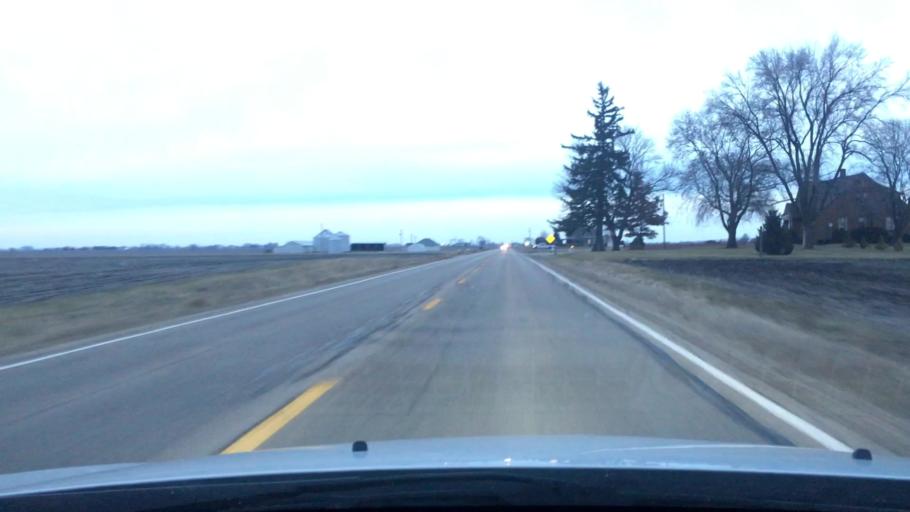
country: US
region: Illinois
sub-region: LaSalle County
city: Peru
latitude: 41.4086
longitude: -89.1261
